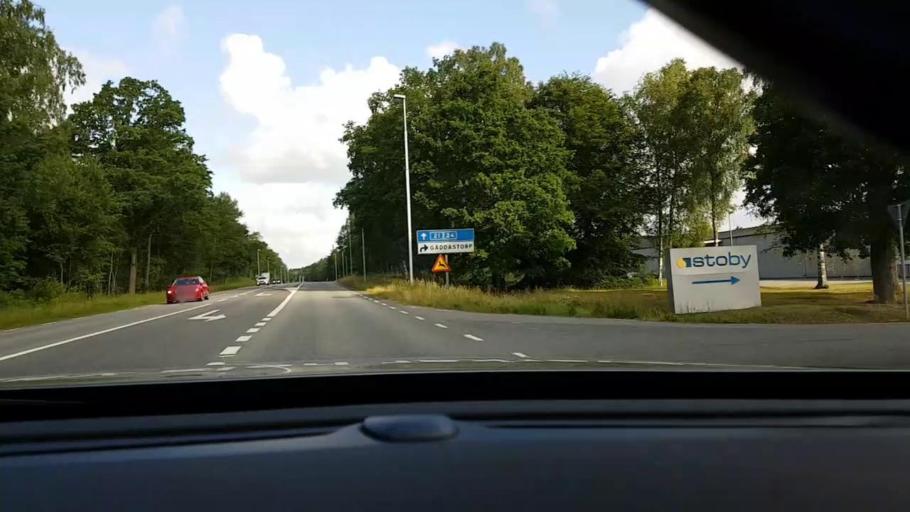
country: SE
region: Skane
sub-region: Hassleholms Kommun
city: Hassleholm
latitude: 56.1631
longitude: 13.7354
